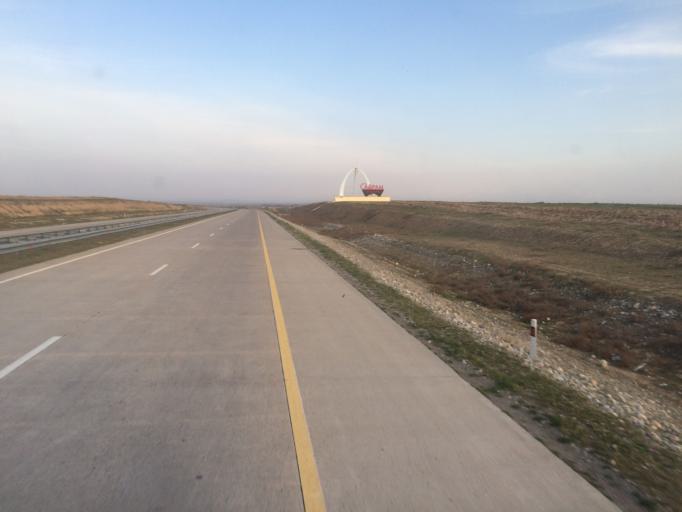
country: KZ
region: Ongtustik Qazaqstan
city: Shymkent
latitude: 42.4936
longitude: 69.4755
